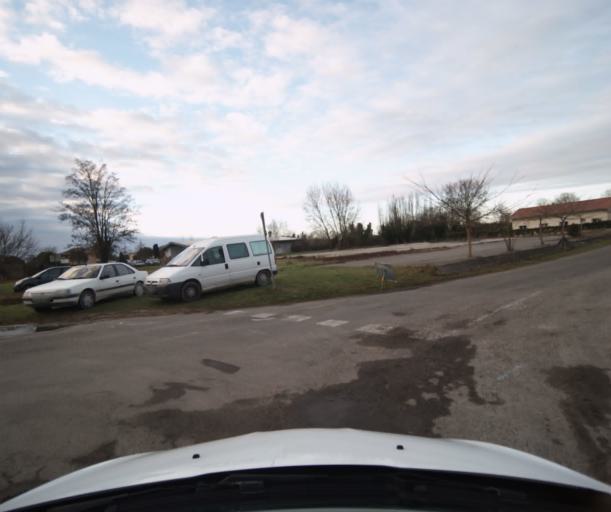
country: FR
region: Midi-Pyrenees
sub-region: Departement du Tarn-et-Garonne
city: Castelsarrasin
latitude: 44.0552
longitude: 1.1047
